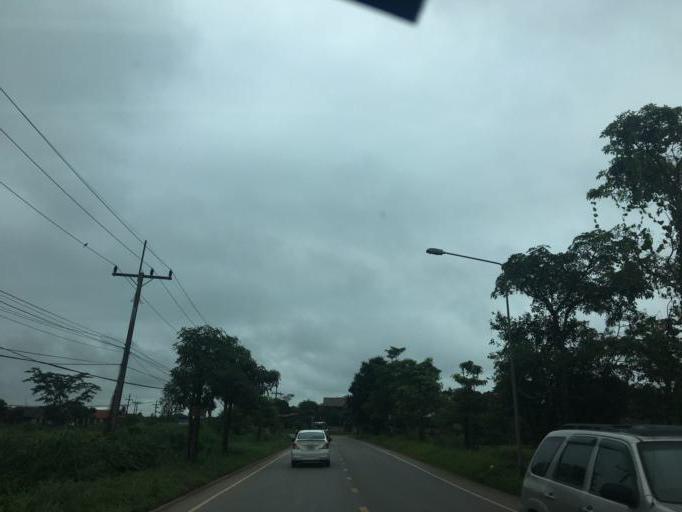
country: TH
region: Chiang Rai
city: Chiang Rai
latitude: 20.0044
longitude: 99.8777
